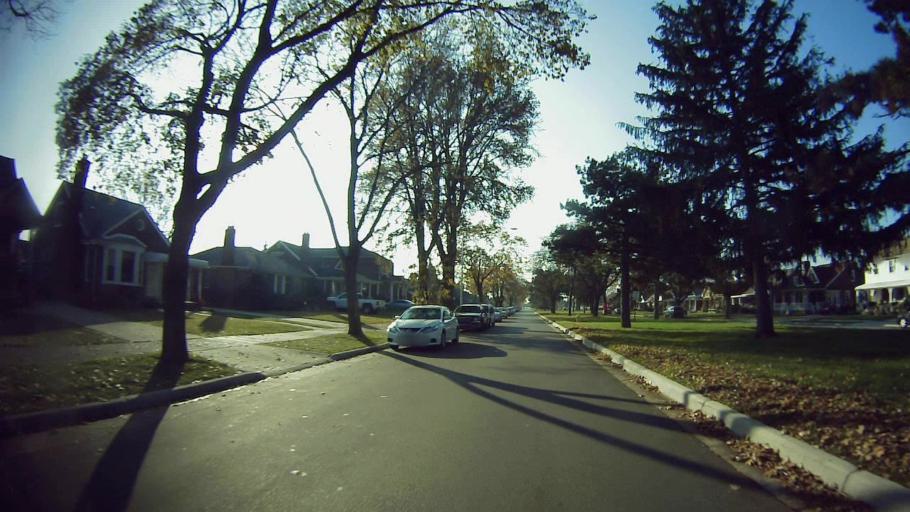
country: US
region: Michigan
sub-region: Wayne County
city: Dearborn
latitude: 42.3341
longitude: -83.1690
